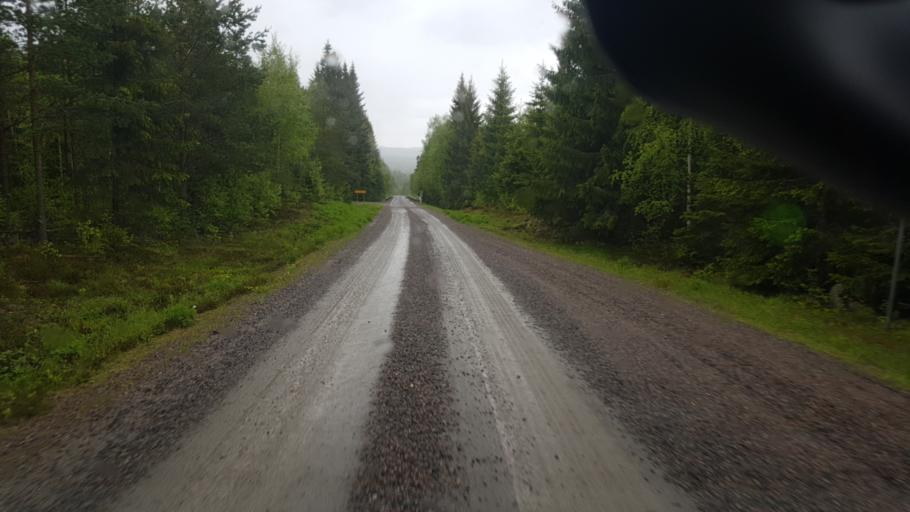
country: SE
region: Vaermland
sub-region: Eda Kommun
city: Charlottenberg
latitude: 59.9817
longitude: 12.4131
